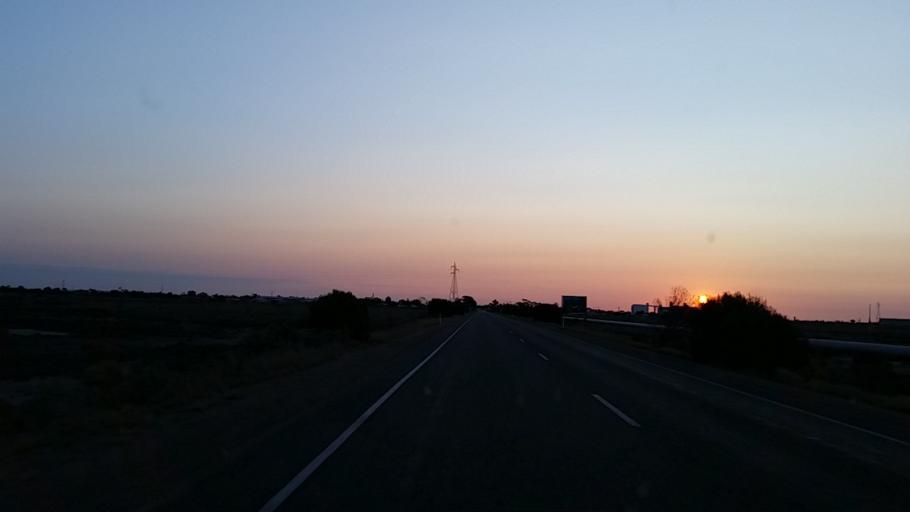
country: AU
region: South Australia
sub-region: Port Pirie City and Dists
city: Solomontown
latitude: -33.1803
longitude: 138.0424
